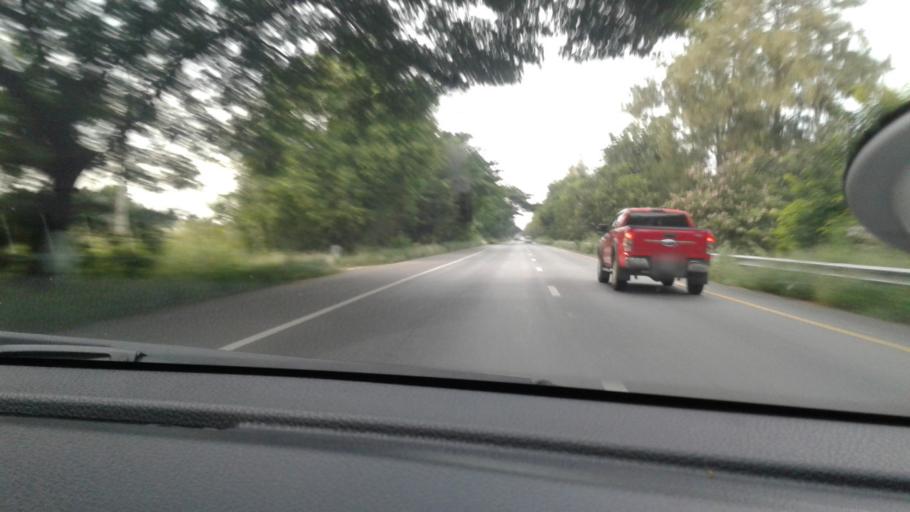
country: TH
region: Prachuap Khiri Khan
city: Hua Hin
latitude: 12.5037
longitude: 99.8861
